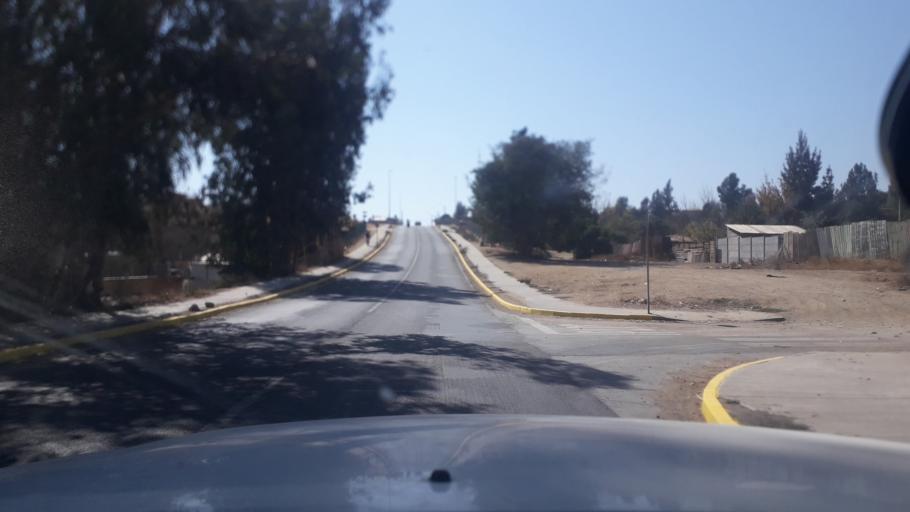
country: CL
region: Valparaiso
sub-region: Provincia de Marga Marga
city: Villa Alemana
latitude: -33.0675
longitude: -71.4036
